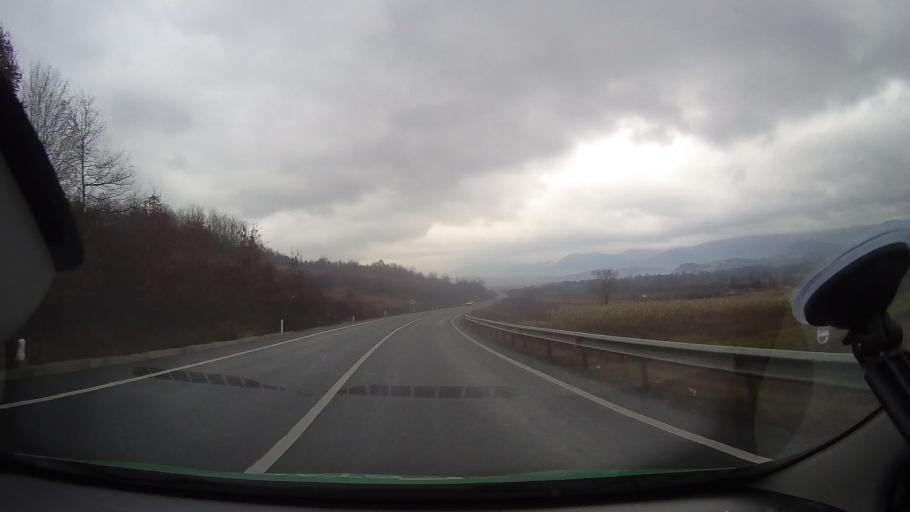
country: RO
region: Hunedoara
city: Vata de Jos
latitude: 46.2060
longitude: 22.5850
